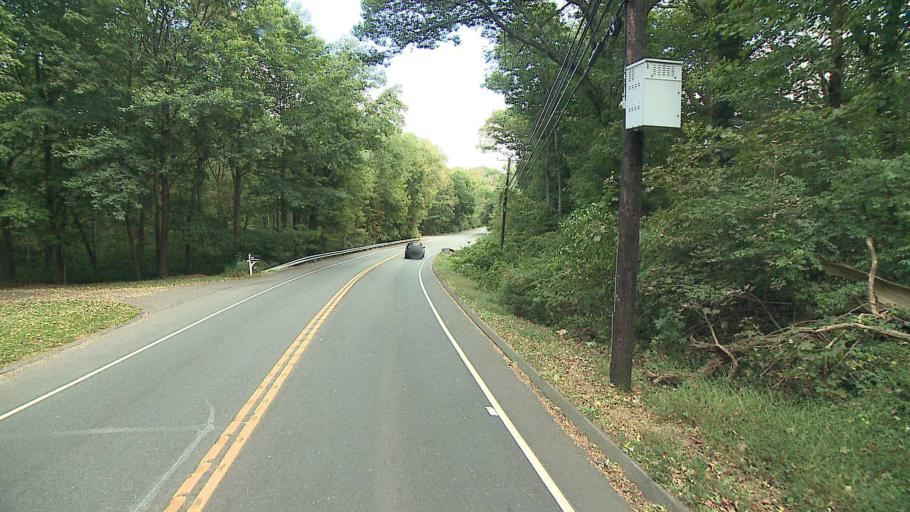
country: US
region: Connecticut
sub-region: Fairfield County
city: Westport
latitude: 41.1750
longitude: -73.3923
